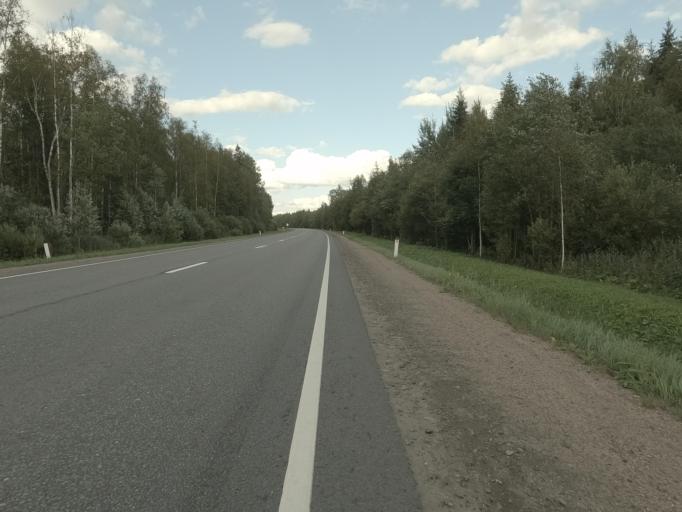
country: RU
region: Leningrad
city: Pavlovo
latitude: 59.6797
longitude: 30.9457
